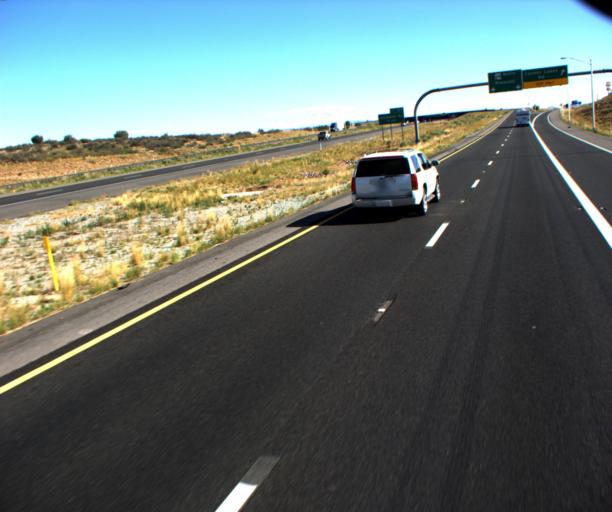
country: US
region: Arizona
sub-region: Yavapai County
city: Cordes Lakes
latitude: 34.3215
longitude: -112.1224
